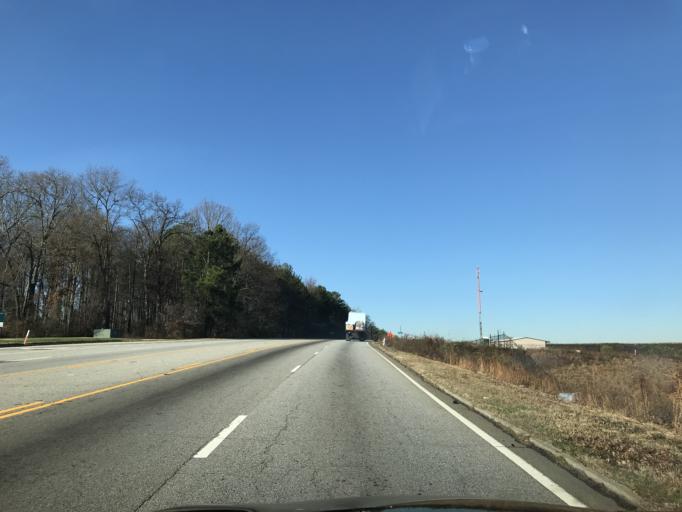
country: US
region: Georgia
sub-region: Fulton County
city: Hapeville
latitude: 33.6179
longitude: -84.4135
